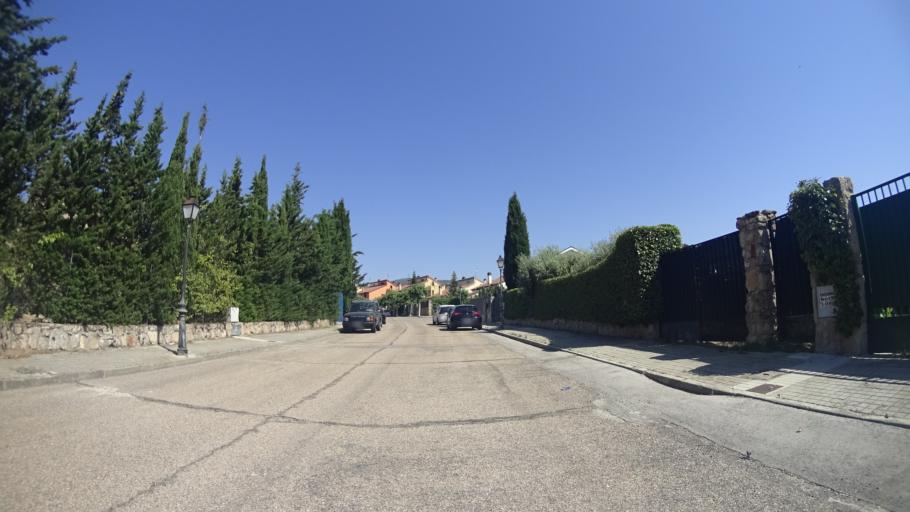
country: ES
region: Madrid
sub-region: Provincia de Madrid
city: Hoyo de Manzanares
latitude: 40.6061
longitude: -3.8981
